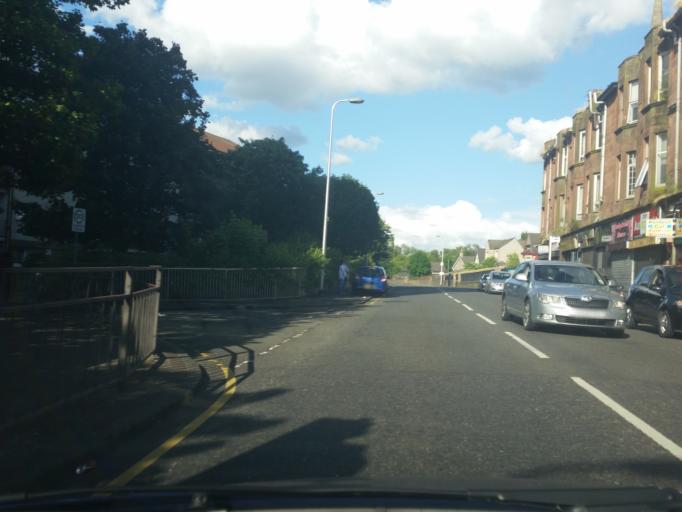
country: GB
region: Scotland
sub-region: North Lanarkshire
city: Coatbridge
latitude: 55.8518
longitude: -4.0195
